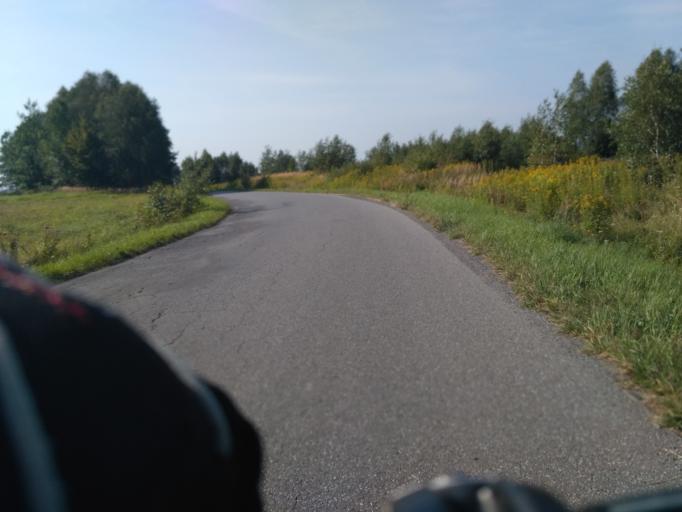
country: PL
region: Subcarpathian Voivodeship
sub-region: Powiat brzozowski
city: Golcowa
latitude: 49.8017
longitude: 22.0252
